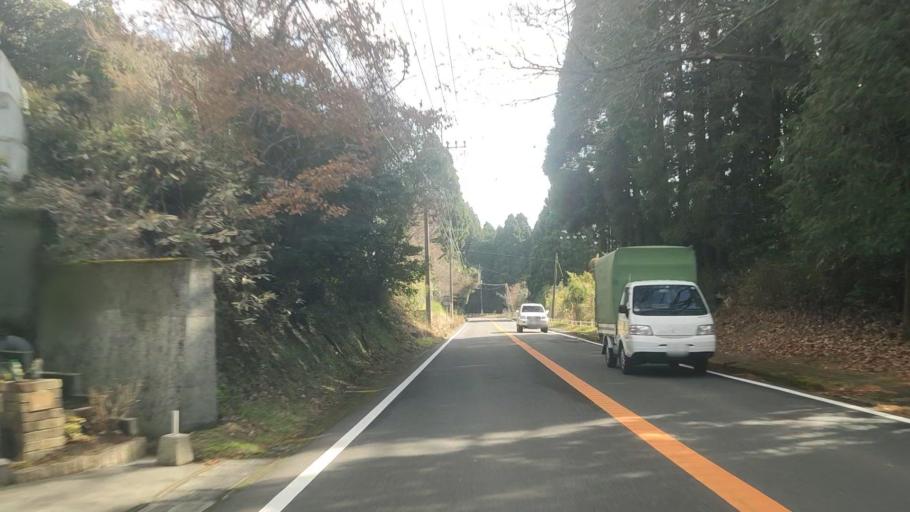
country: JP
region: Kagoshima
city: Kajiki
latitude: 31.8250
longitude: 130.6907
